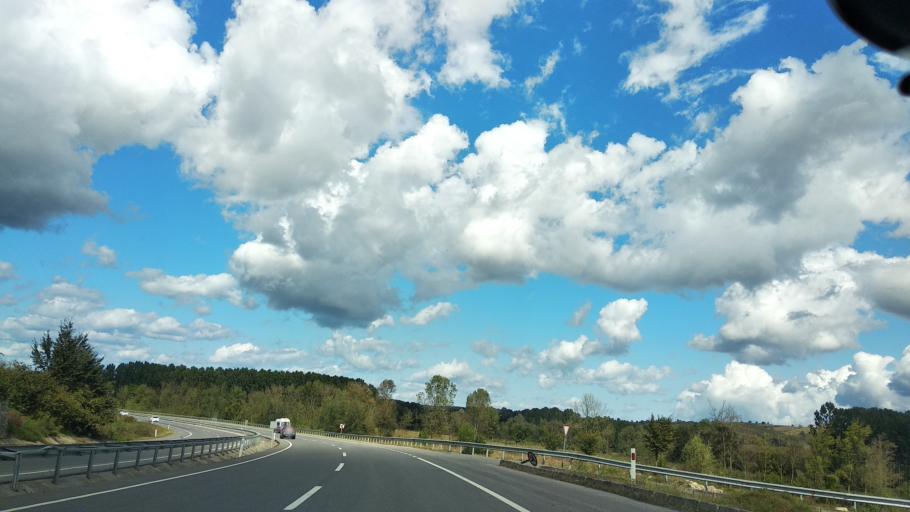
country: TR
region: Sakarya
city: Ortakoy
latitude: 41.0073
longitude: 30.6122
